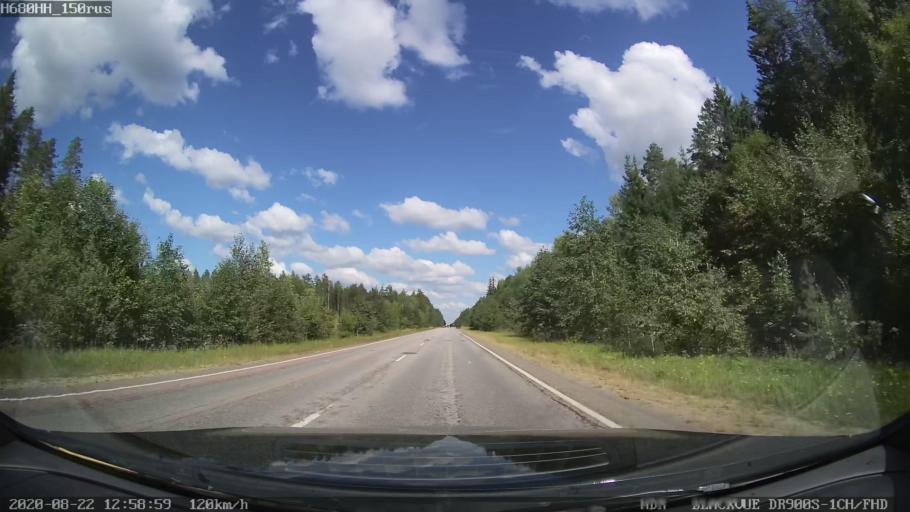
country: RU
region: Tverskaya
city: Bezhetsk
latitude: 57.5987
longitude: 36.3532
